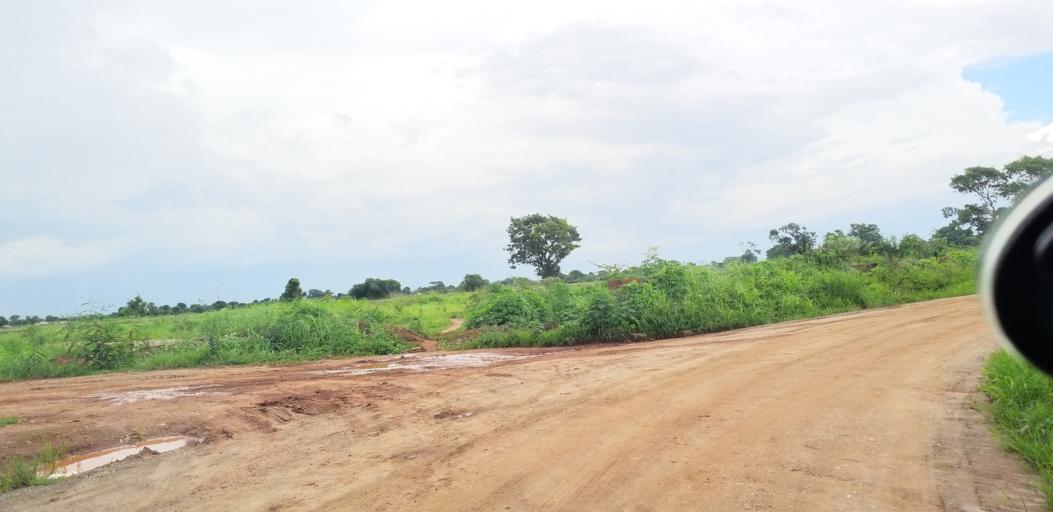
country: ZM
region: Lusaka
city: Lusaka
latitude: -15.5212
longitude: 28.3106
